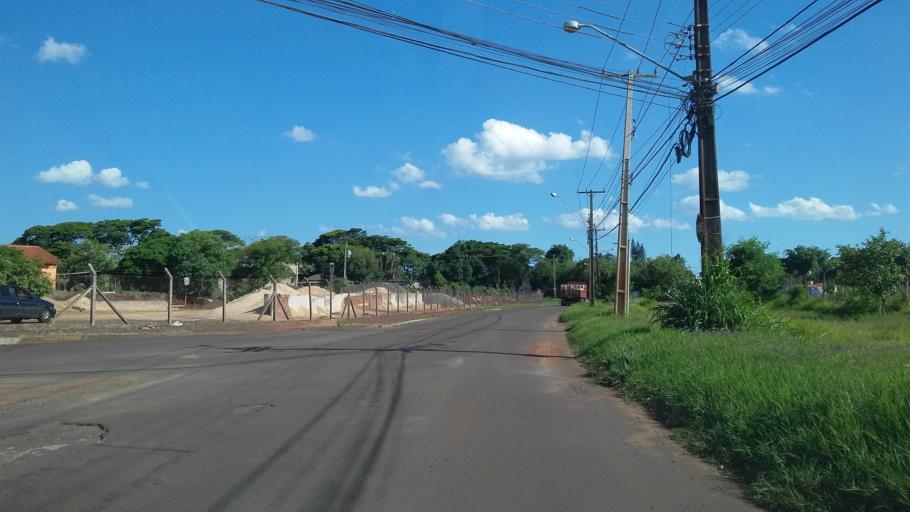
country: BR
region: Parana
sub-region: Londrina
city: Londrina
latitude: -23.2886
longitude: -51.2091
